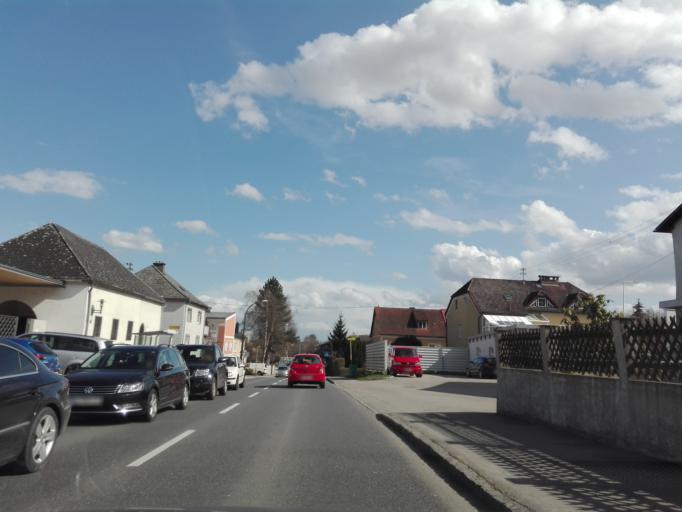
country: AT
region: Upper Austria
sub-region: Politischer Bezirk Urfahr-Umgebung
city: Feldkirchen an der Donau
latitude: 48.3642
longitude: 14.0216
